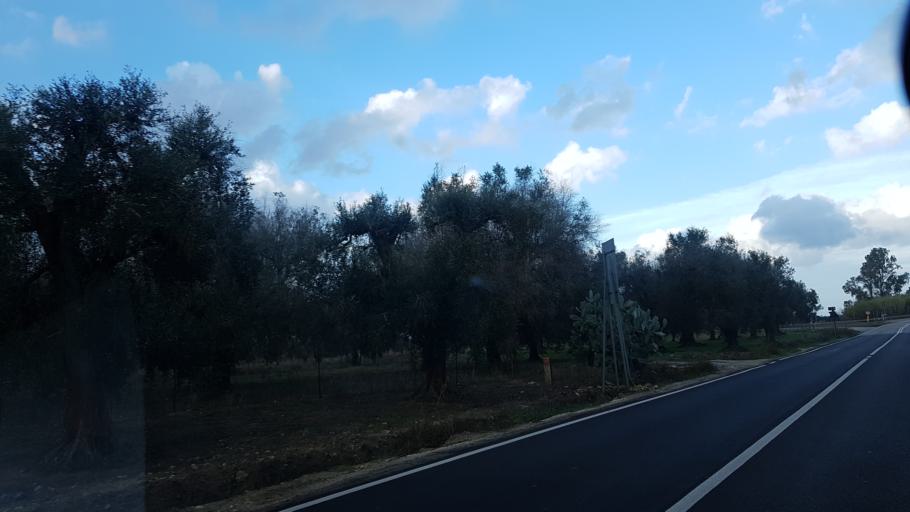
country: IT
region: Apulia
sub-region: Provincia di Brindisi
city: San Pietro Vernotico
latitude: 40.5185
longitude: 18.0138
